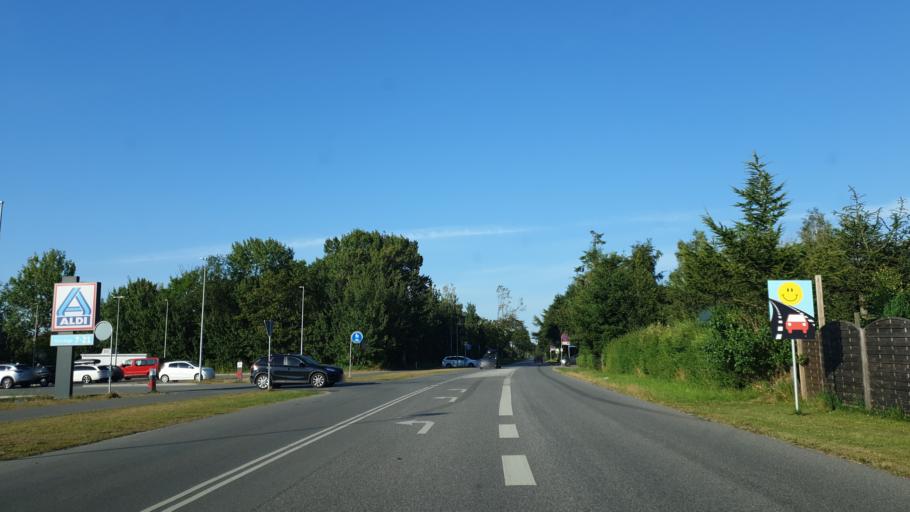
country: DK
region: Zealand
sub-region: Guldborgsund Kommune
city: Nykobing Falster
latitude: 54.7038
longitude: 11.9664
